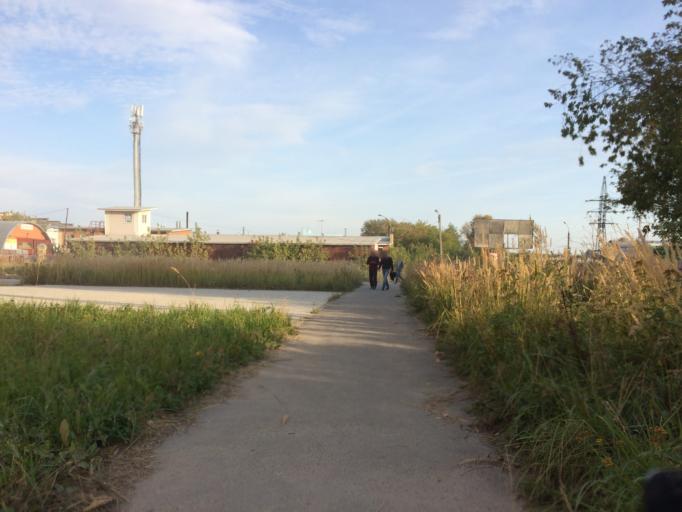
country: RU
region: Mariy-El
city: Yoshkar-Ola
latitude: 56.6267
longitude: 47.8495
